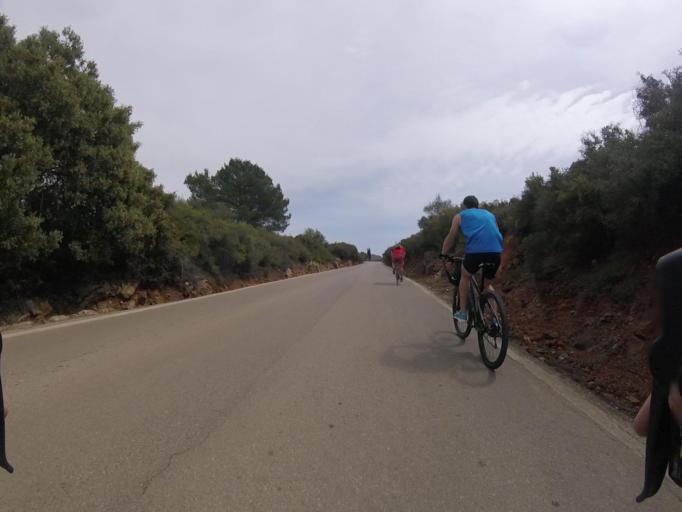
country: ES
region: Valencia
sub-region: Provincia de Castello
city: Cabanes
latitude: 40.1563
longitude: 0.0611
